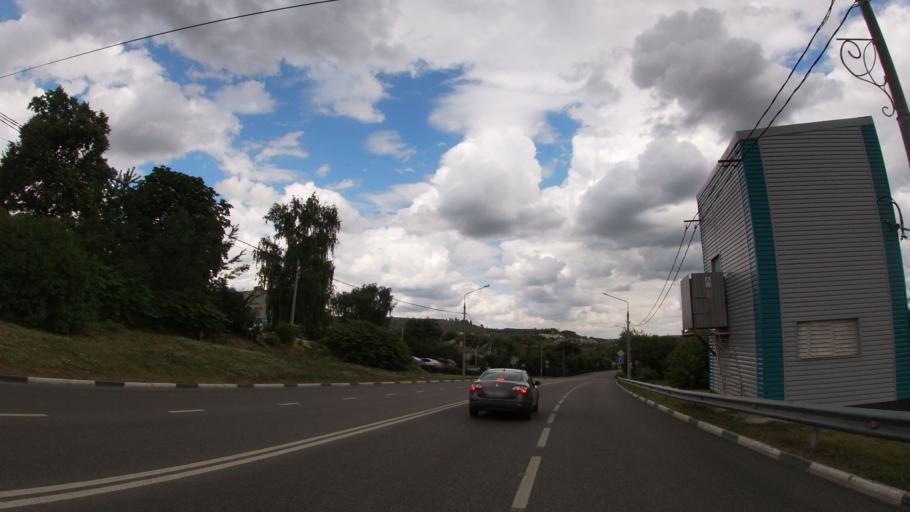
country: RU
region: Belgorod
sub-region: Belgorodskiy Rayon
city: Belgorod
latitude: 50.6049
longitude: 36.6108
